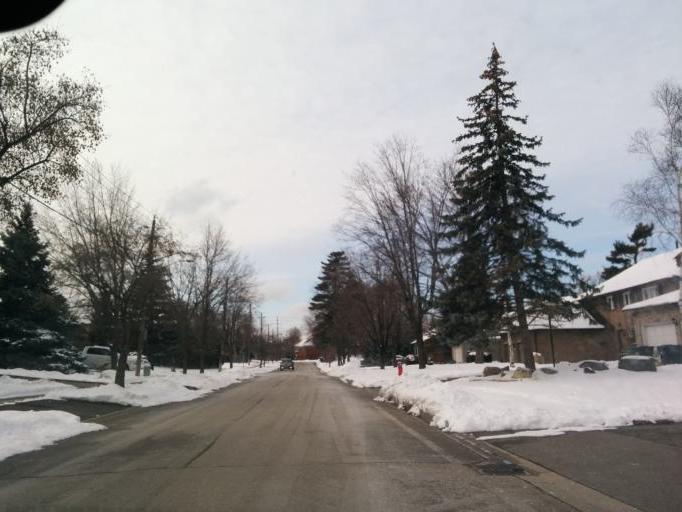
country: CA
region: Ontario
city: Mississauga
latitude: 43.5368
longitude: -79.6620
